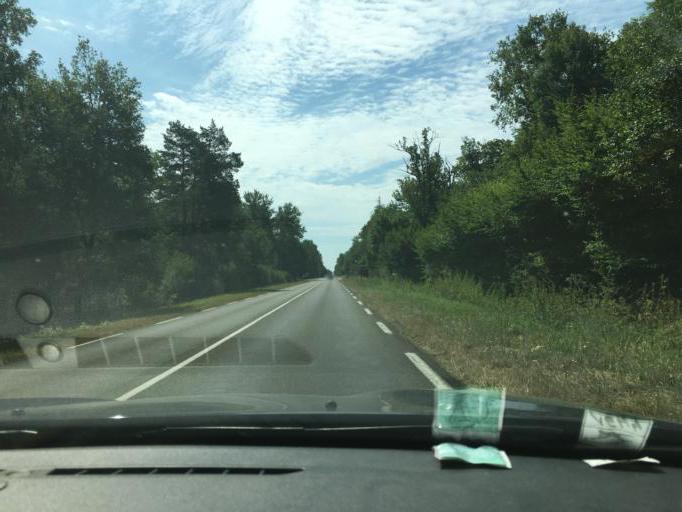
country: FR
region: Centre
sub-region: Departement du Loiret
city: La Ferte-Saint-Aubin
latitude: 47.6757
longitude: 1.9685
